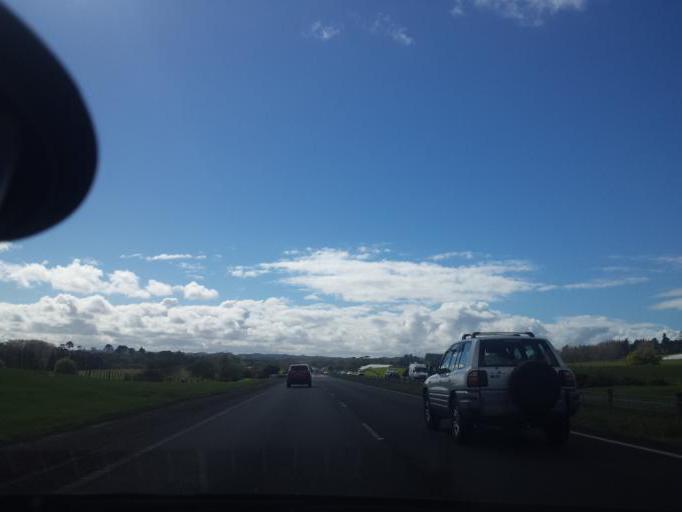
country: NZ
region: Auckland
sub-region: Auckland
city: Rothesay Bay
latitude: -36.6409
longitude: 174.6626
